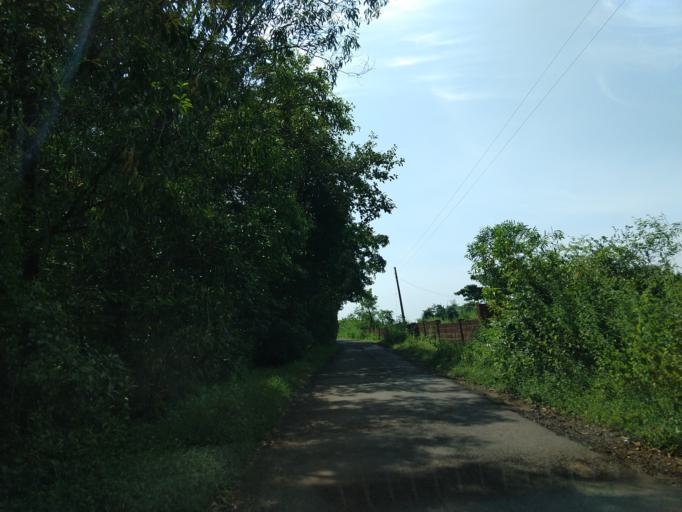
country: IN
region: Maharashtra
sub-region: Sindhudurg
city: Kudal
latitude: 16.0477
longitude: 73.6810
